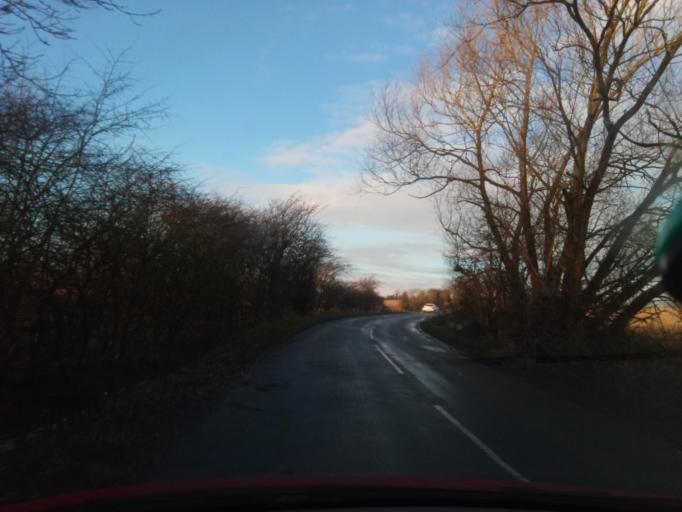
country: GB
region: England
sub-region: Derbyshire
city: Melbourne
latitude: 52.8551
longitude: -1.4366
